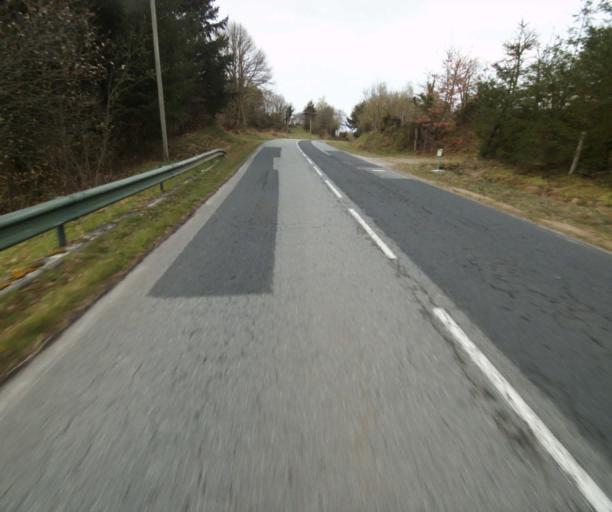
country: FR
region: Limousin
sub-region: Departement de la Correze
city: Correze
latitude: 45.3824
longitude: 1.8645
